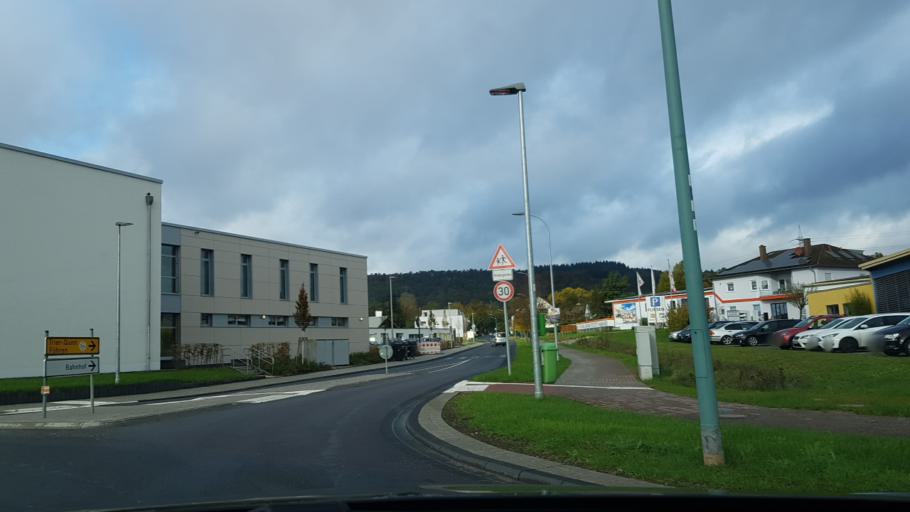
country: DE
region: Rheinland-Pfalz
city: Schweich
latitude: 49.8283
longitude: 6.7423
